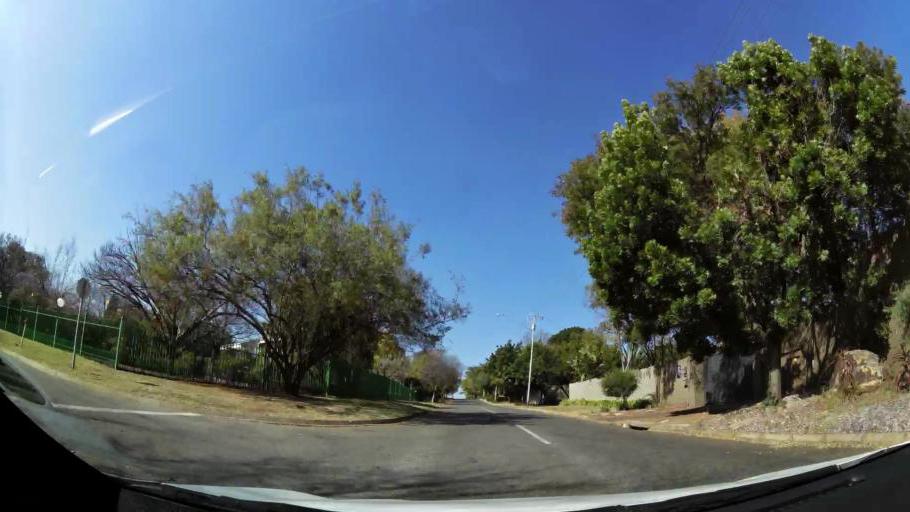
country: ZA
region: Gauteng
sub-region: City of Tshwane Metropolitan Municipality
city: Pretoria
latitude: -25.7998
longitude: 28.2278
